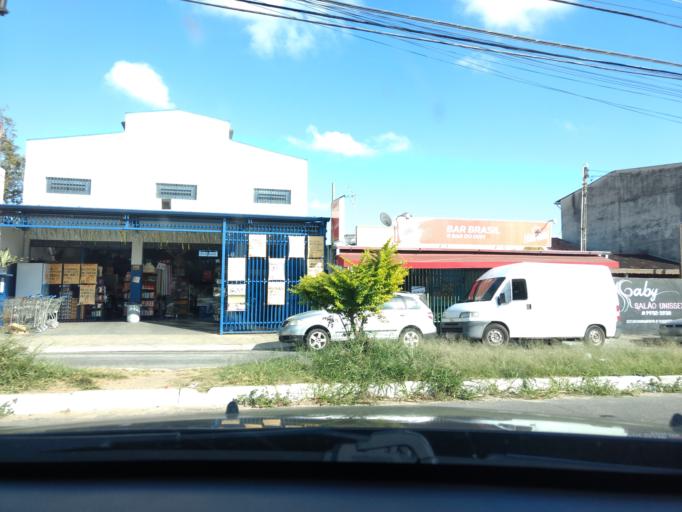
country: BR
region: Sao Paulo
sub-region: Taubate
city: Taubate
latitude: -23.0069
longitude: -45.5270
